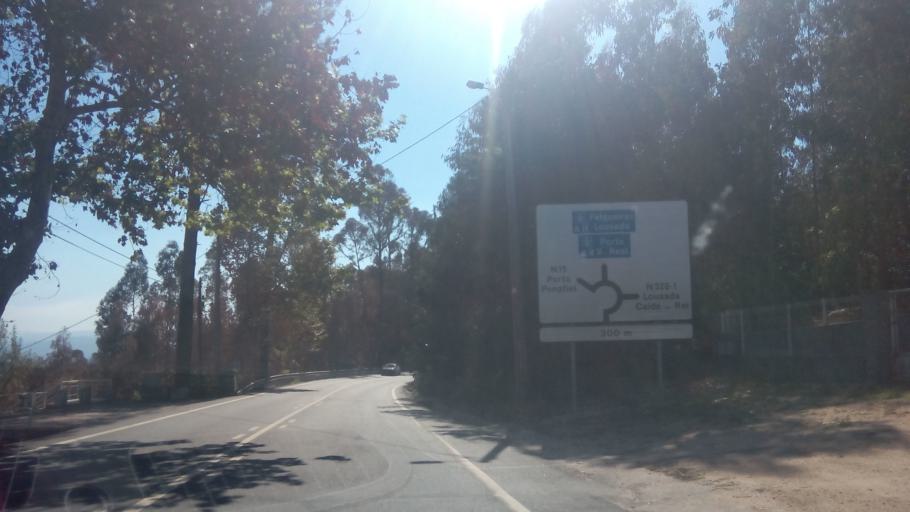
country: PT
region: Porto
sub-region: Lousada
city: Meinedo
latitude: 41.2611
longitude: -8.2099
